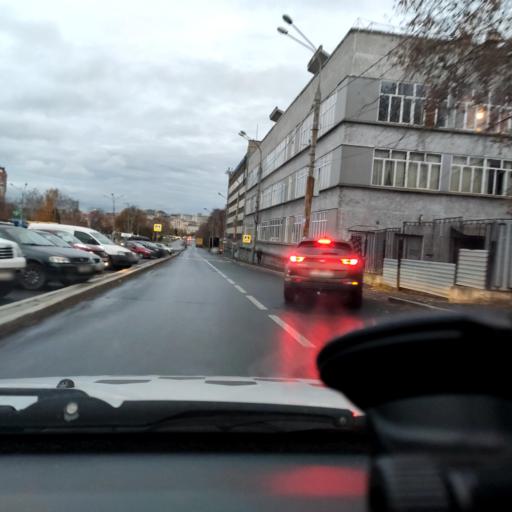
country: RU
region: Perm
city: Perm
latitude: 58.0039
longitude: 56.1851
